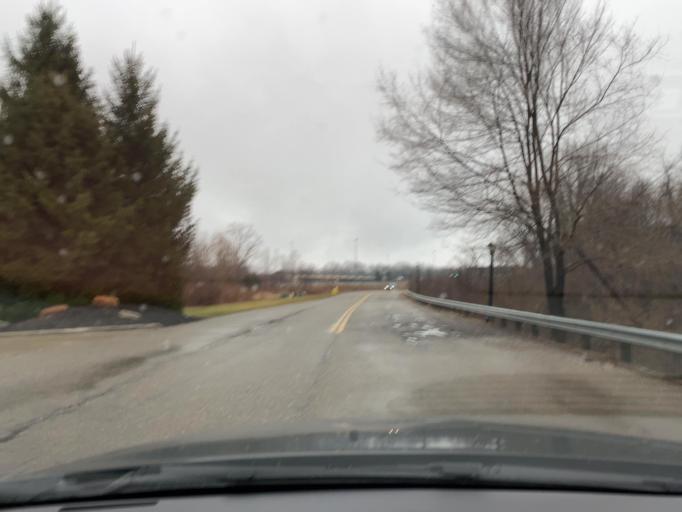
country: US
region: Ohio
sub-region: Summit County
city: Fairlawn
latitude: 41.1008
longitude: -81.5916
